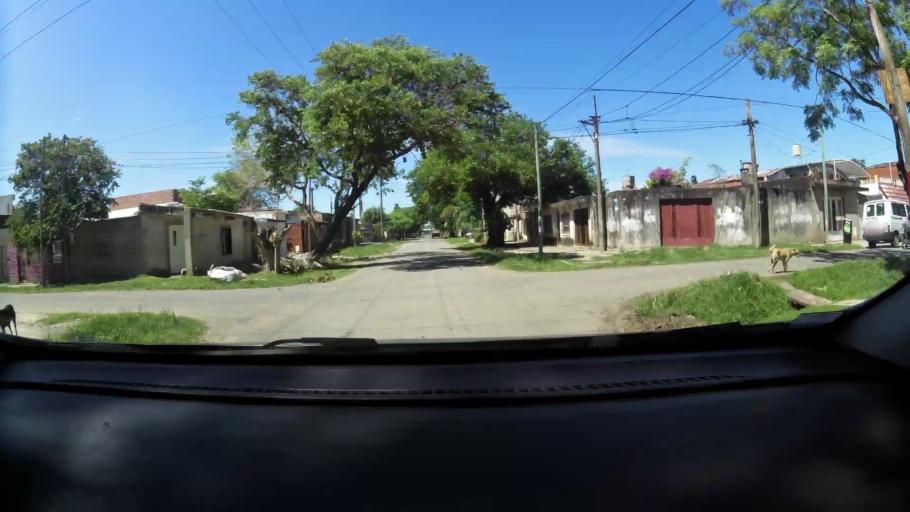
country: AR
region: Santa Fe
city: Perez
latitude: -32.9540
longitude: -60.7155
